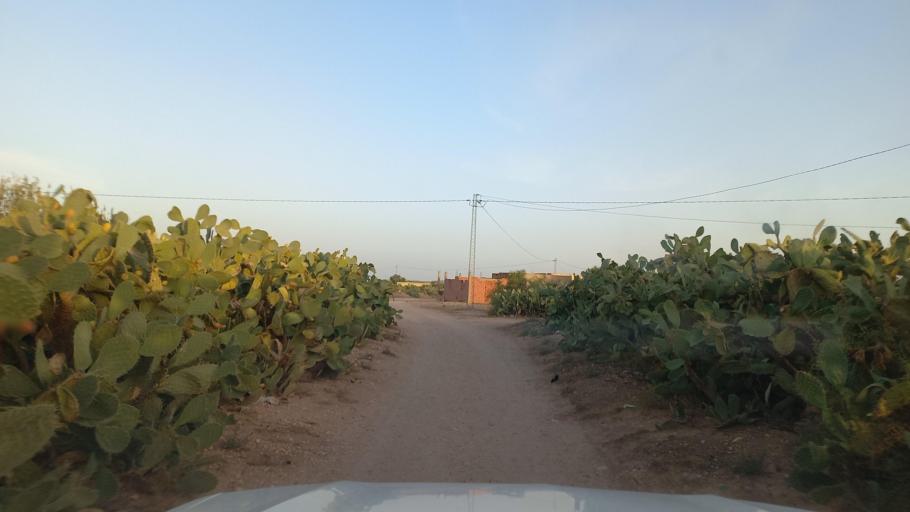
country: TN
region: Al Qasrayn
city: Kasserine
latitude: 35.2409
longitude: 8.9907
